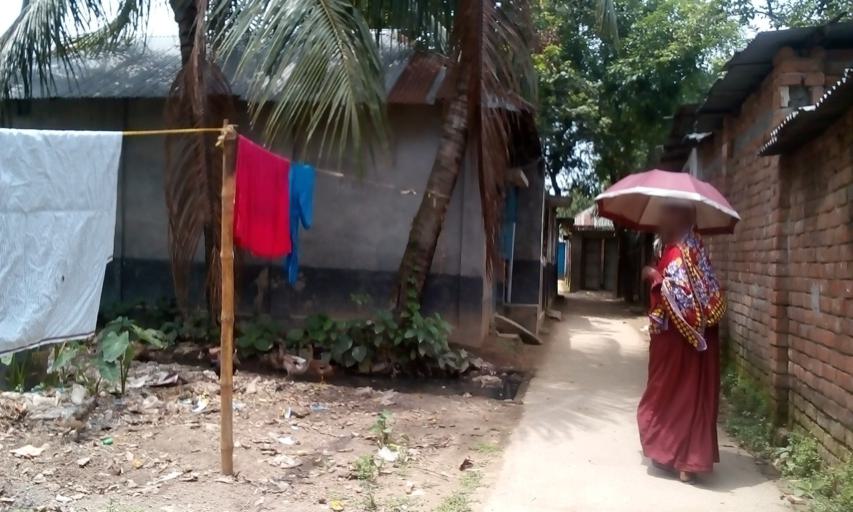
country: BD
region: Rangpur Division
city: Parbatipur
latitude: 25.4016
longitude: 88.9908
